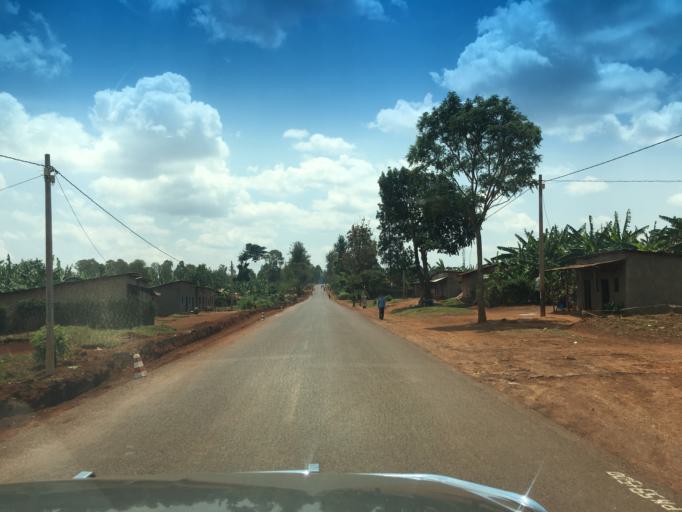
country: RW
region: Eastern Province
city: Kibungo
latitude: -2.2745
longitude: 30.6068
